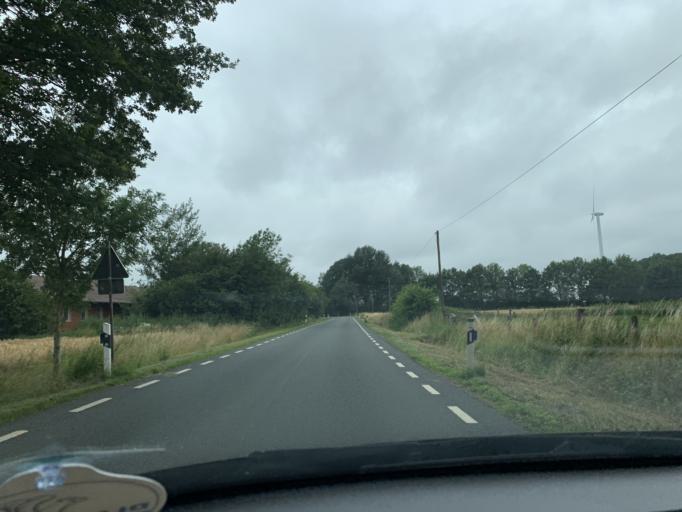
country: DE
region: North Rhine-Westphalia
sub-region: Regierungsbezirk Munster
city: Laer
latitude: 52.0448
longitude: 7.3826
